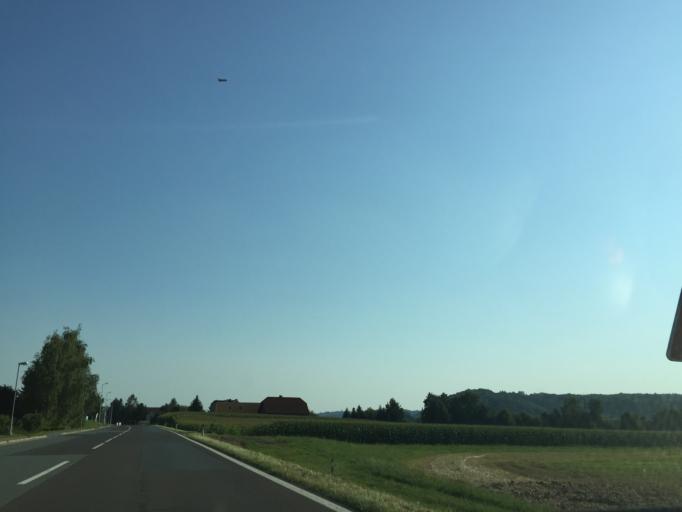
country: AT
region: Styria
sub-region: Politischer Bezirk Suedoststeiermark
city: Merkendorf
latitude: 46.8612
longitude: 15.9026
